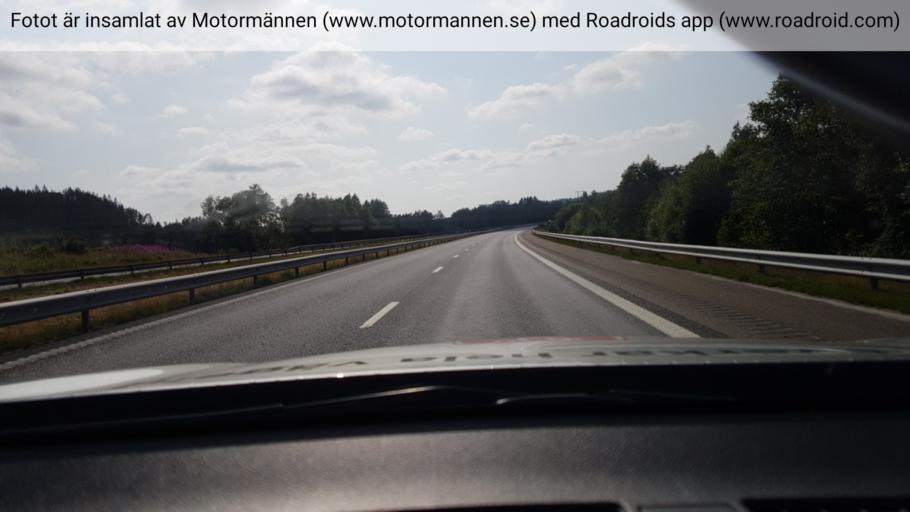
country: SE
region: Vaestra Goetaland
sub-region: Bollebygds Kommun
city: Bollebygd
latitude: 57.6617
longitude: 12.5656
